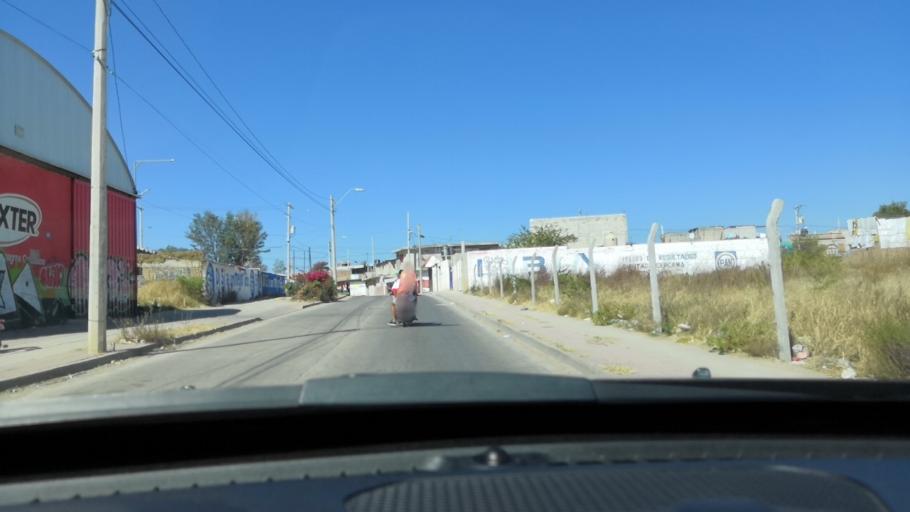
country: MX
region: Guanajuato
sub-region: Leon
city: Centro Familiar la Soledad
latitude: 21.1418
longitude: -101.7537
